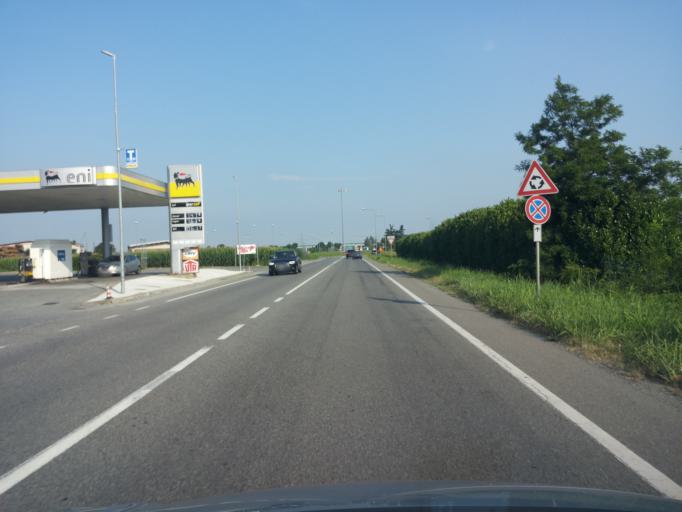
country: IT
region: Piedmont
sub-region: Provincia di Vercelli
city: Santhia
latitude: 45.3870
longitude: 8.1333
